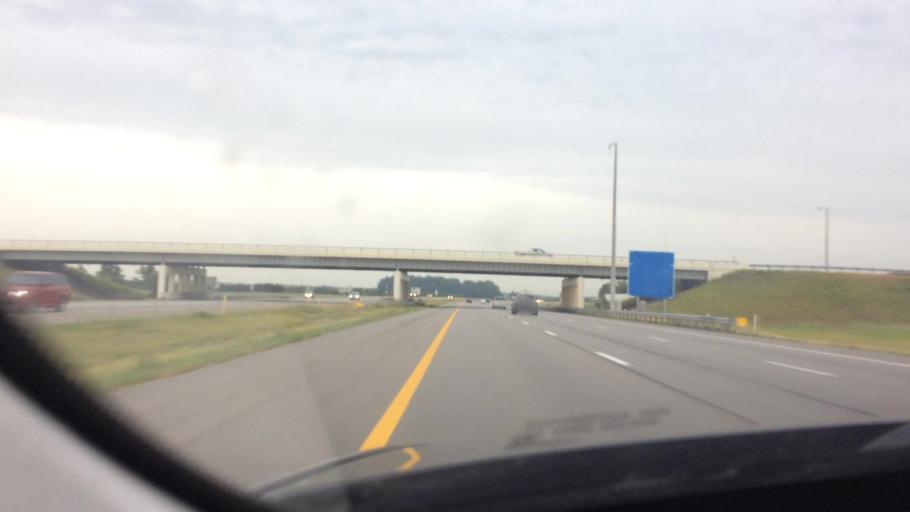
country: US
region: Ohio
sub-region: Wood County
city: Bowling Green
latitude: 41.3756
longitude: -83.6163
